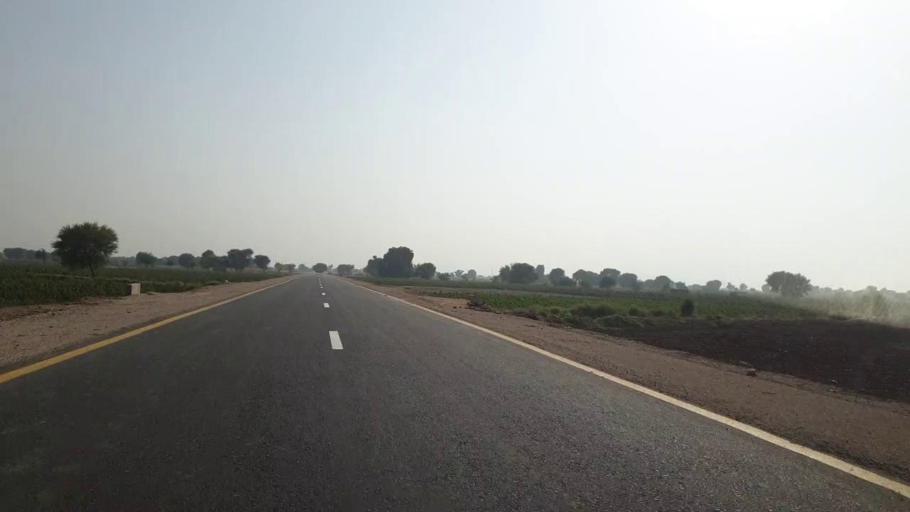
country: PK
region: Sindh
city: Bhan
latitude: 26.5125
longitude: 67.7854
